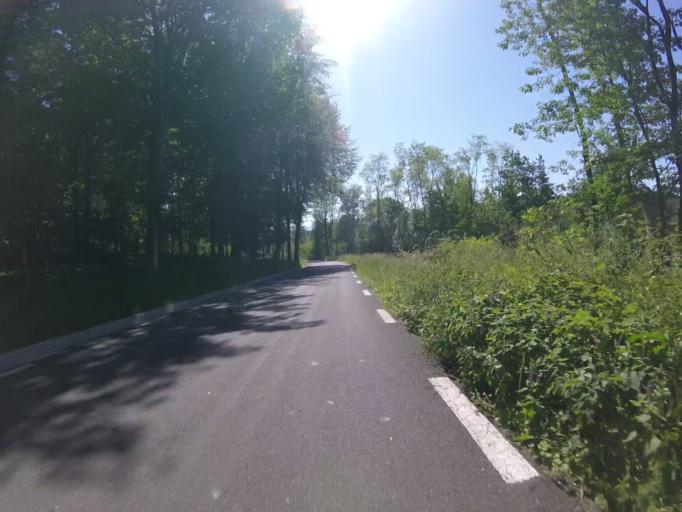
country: ES
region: Basque Country
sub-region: Provincia de Guipuzcoa
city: Beizama
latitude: 43.1234
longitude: -2.1747
